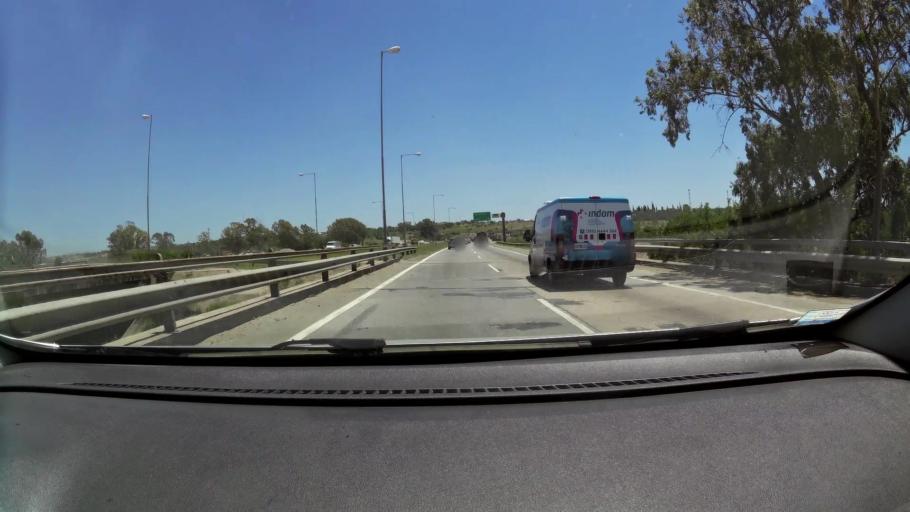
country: AR
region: Cordoba
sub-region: Departamento de Capital
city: Cordoba
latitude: -31.4026
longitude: -64.1262
